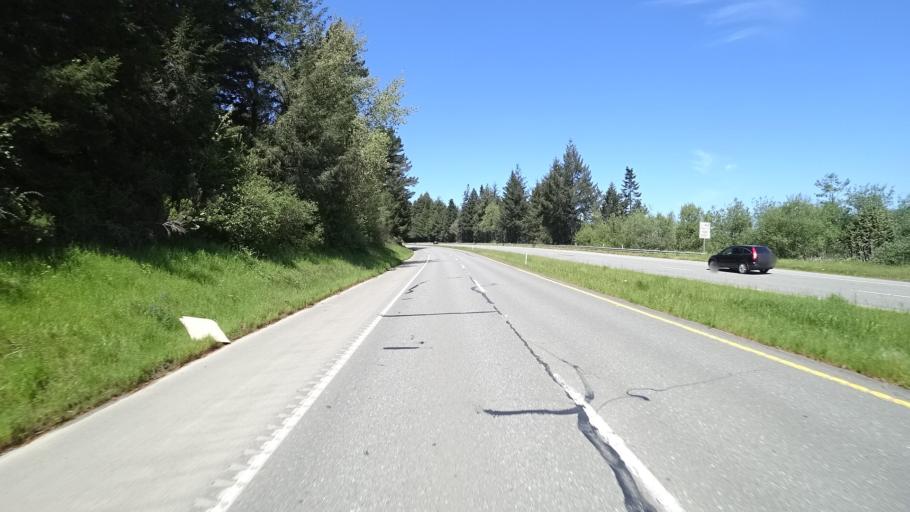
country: US
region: California
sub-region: Humboldt County
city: Blue Lake
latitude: 40.9048
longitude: -124.0291
